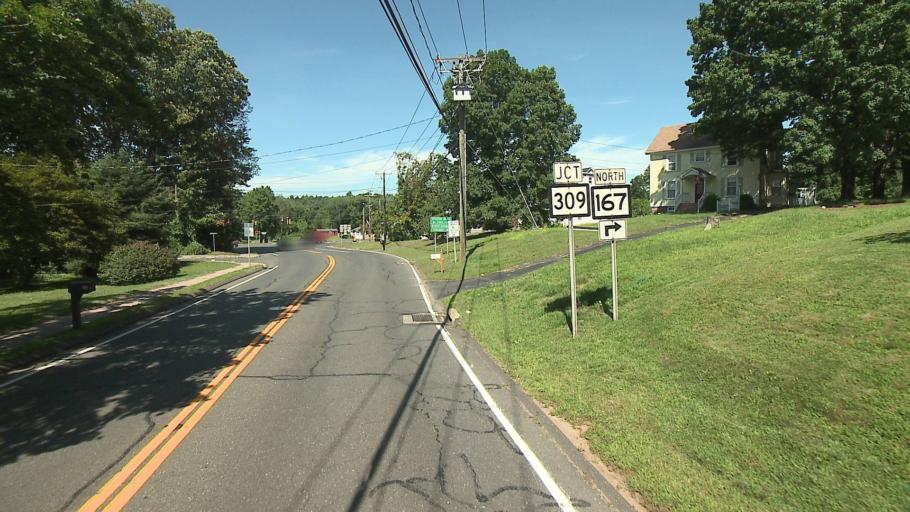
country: US
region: Connecticut
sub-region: Hartford County
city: Simsbury Center
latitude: 41.8690
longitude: -72.8186
